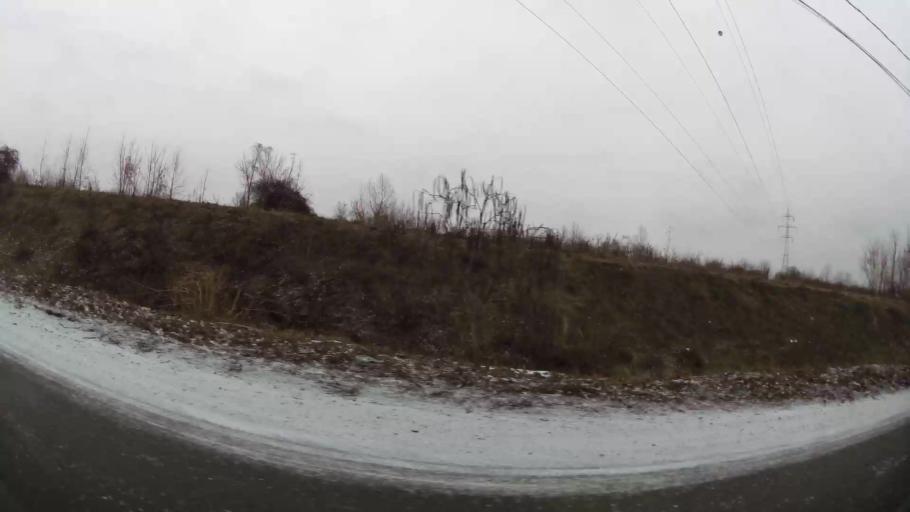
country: RO
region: Dambovita
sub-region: Municipiul Targoviste
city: Targoviste
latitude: 44.9290
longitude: 25.4798
